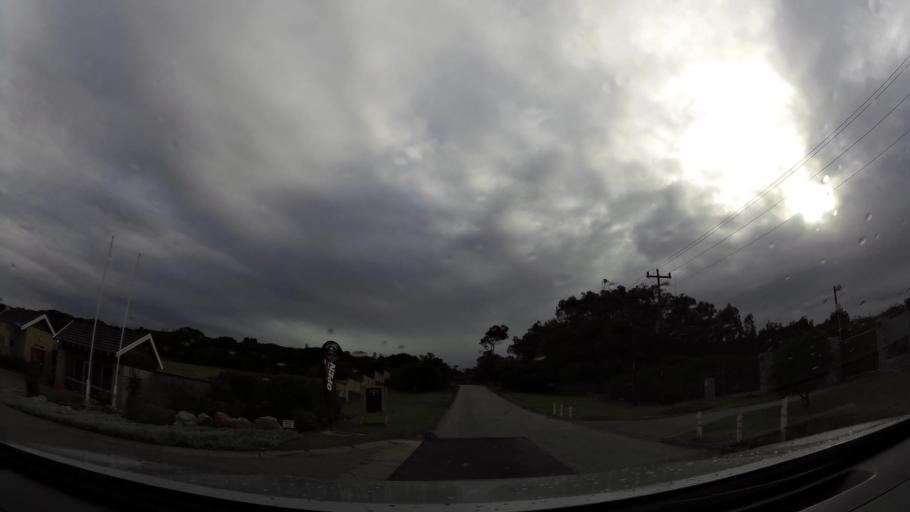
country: ZA
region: Eastern Cape
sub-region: Nelson Mandela Bay Metropolitan Municipality
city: Port Elizabeth
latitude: -34.0150
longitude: 25.4973
